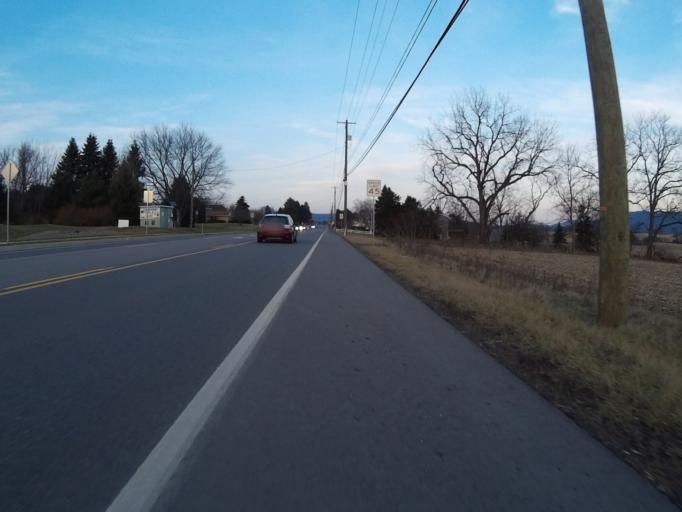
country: US
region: Pennsylvania
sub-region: Centre County
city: Pine Grove Mills
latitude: 40.7623
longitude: -77.8736
